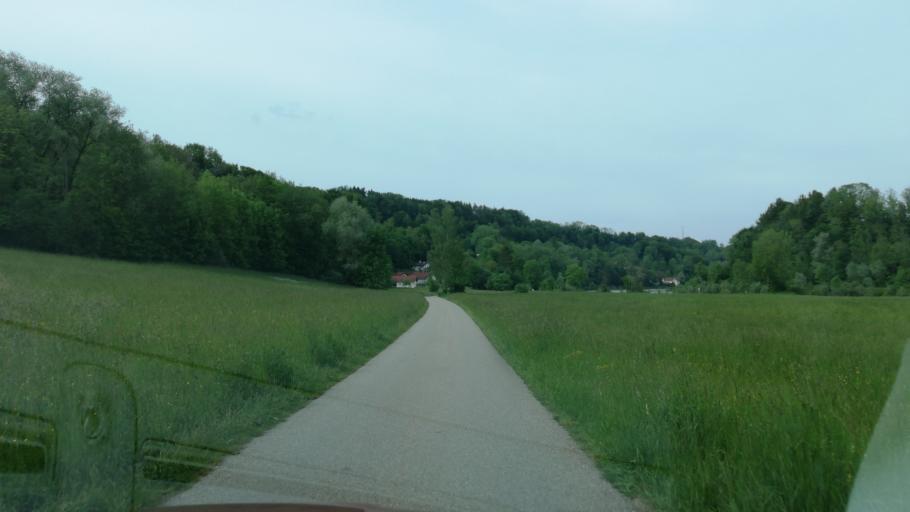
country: DE
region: Bavaria
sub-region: Upper Bavaria
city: Mehring
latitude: 48.1408
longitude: 12.7955
